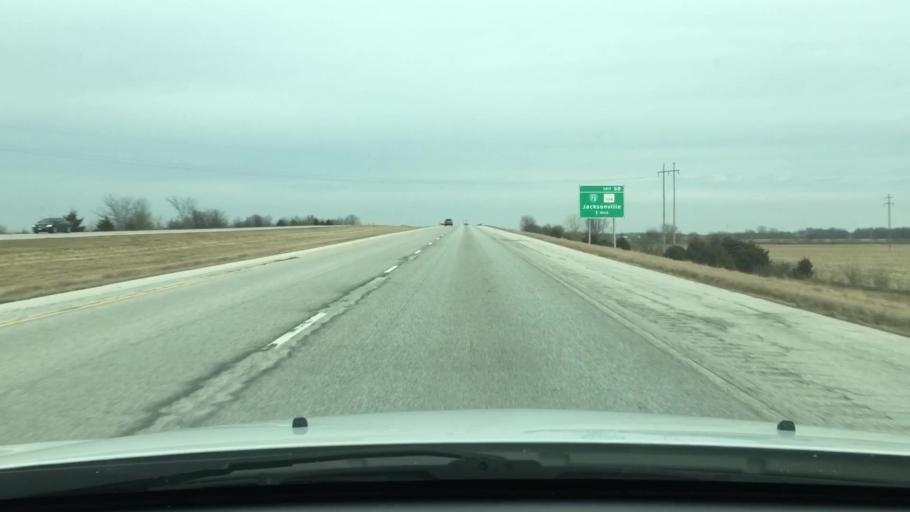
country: US
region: Illinois
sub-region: Morgan County
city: South Jacksonville
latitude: 39.7072
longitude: -90.1836
